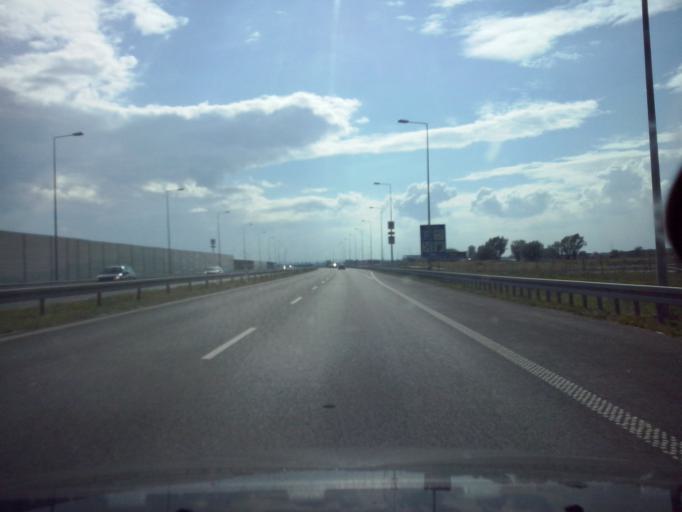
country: PL
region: Lesser Poland Voivodeship
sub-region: Powiat tarnowski
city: Wierzchoslawice
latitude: 50.0453
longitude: 20.8948
